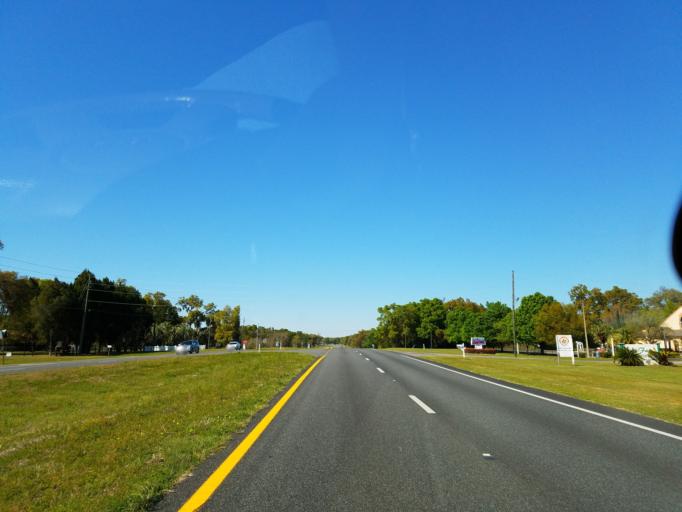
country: US
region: Florida
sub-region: Marion County
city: Belleview
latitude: 29.0423
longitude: -82.0453
